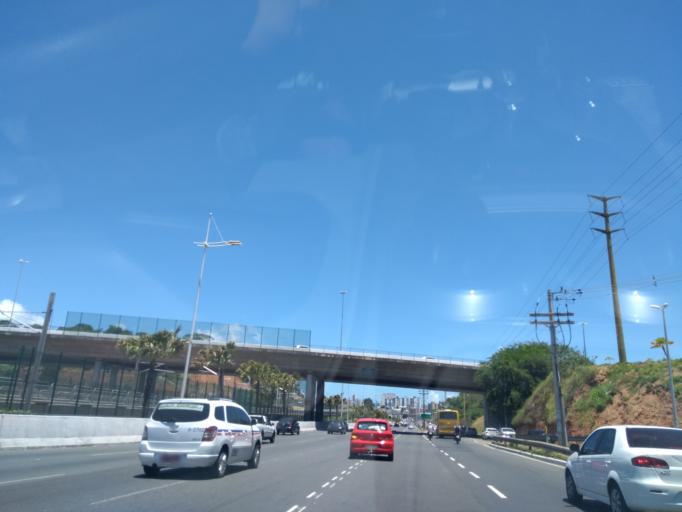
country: BR
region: Bahia
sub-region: Salvador
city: Salvador
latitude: -12.9742
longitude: -38.4503
